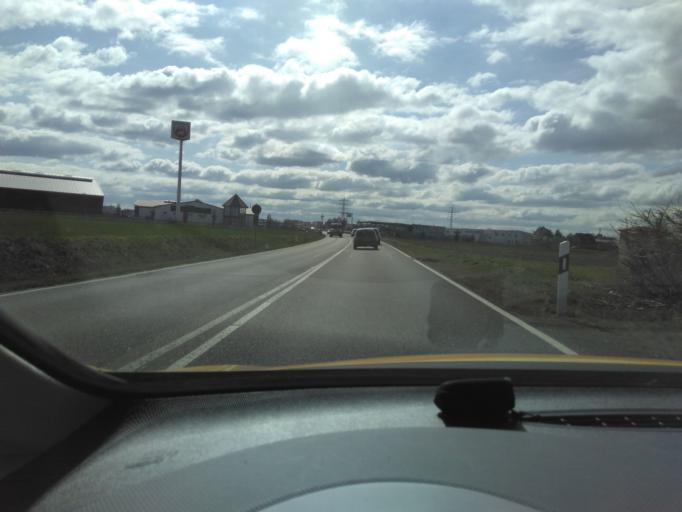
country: DE
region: North Rhine-Westphalia
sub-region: Regierungsbezirk Koln
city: Erftstadt
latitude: 50.8010
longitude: 6.7857
